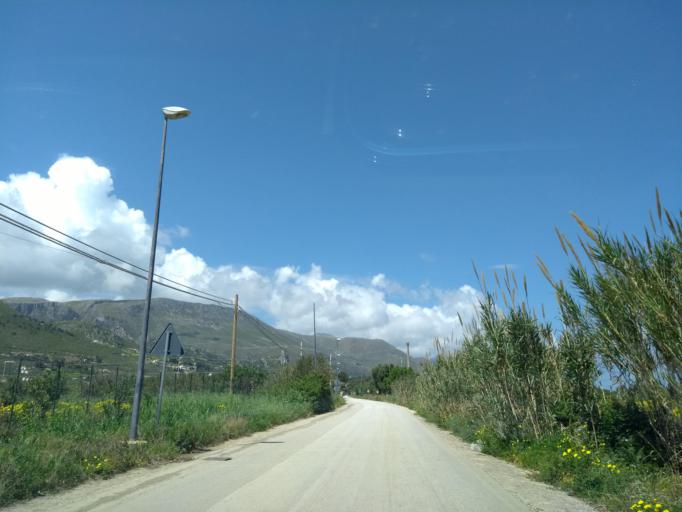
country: IT
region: Sicily
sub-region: Trapani
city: Castellammare del Golfo
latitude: 38.0583
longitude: 12.8324
